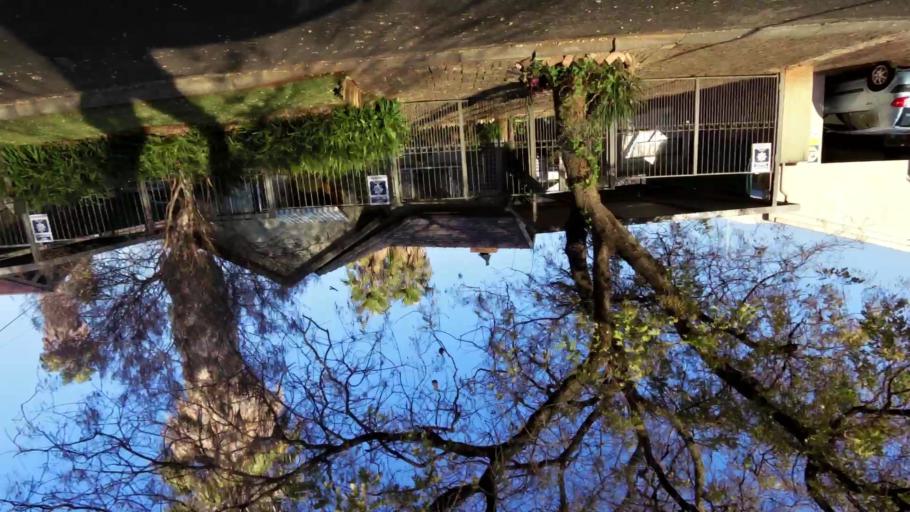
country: ZA
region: Gauteng
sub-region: City of Johannesburg Metropolitan Municipality
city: Johannesburg
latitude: -26.1603
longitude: 27.9853
